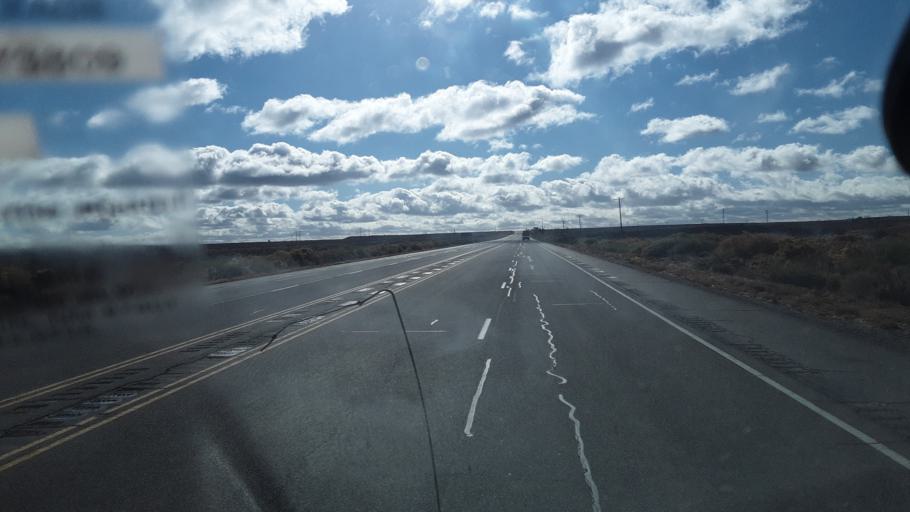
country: US
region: New Mexico
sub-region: San Juan County
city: Lee Acres
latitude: 36.5602
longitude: -107.9830
